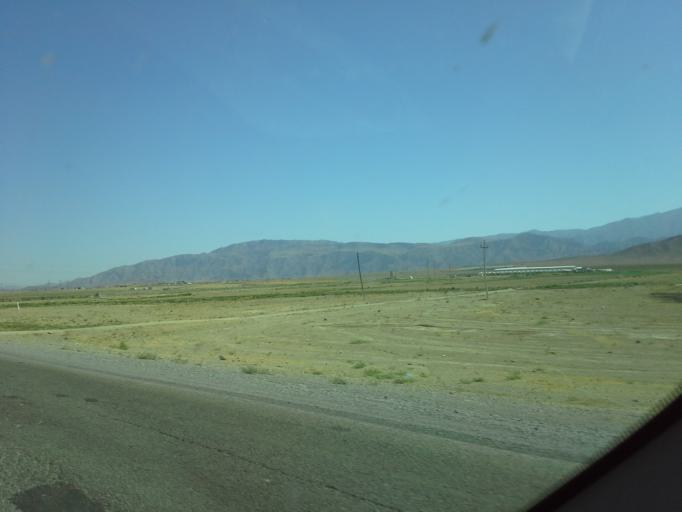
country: TM
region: Ahal
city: Baharly
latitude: 38.4536
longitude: 57.3672
